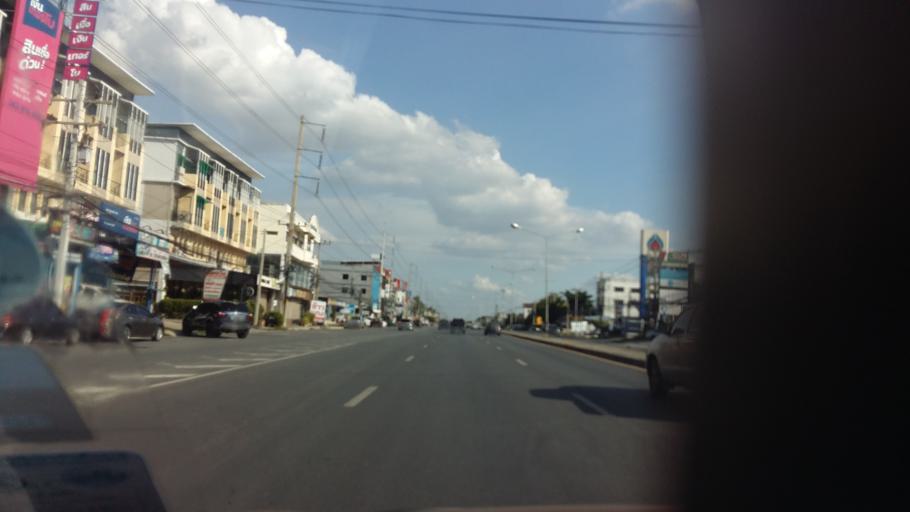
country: TH
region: Lop Buri
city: Lop Buri
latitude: 14.8267
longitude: 100.6471
